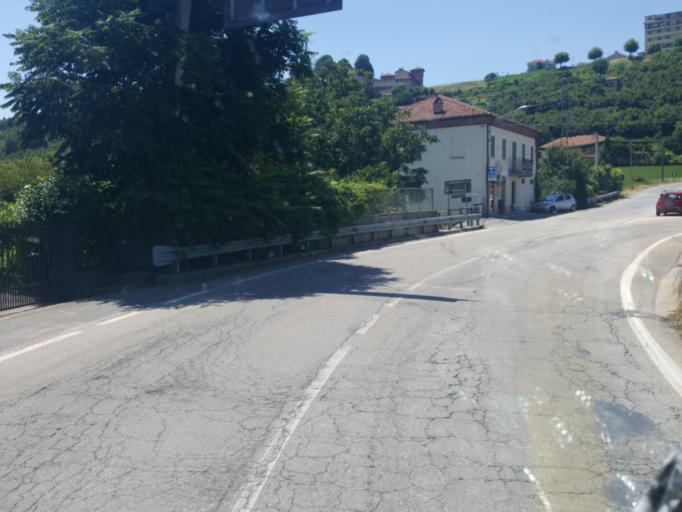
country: IT
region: Piedmont
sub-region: Provincia di Cuneo
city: Cherasco
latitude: 44.6507
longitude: 7.8672
